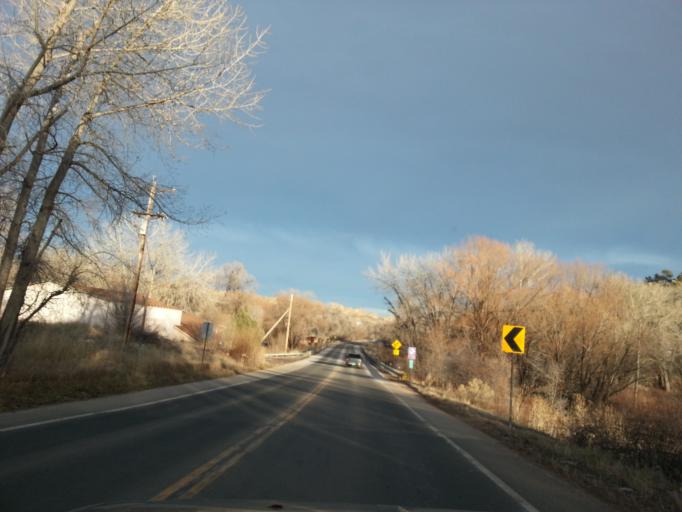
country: US
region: Colorado
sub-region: Larimer County
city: Loveland
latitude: 40.4184
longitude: -105.1819
